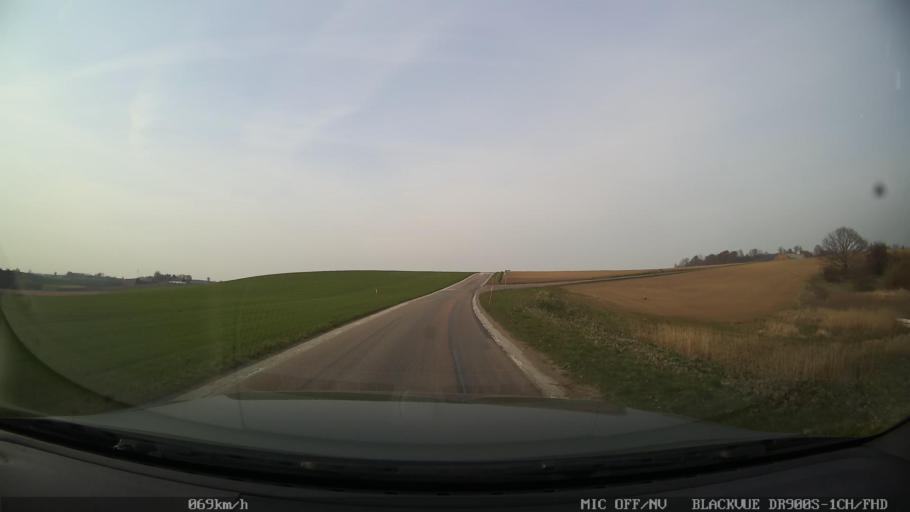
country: SE
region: Skane
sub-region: Ystads Kommun
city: Ystad
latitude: 55.4483
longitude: 13.8320
